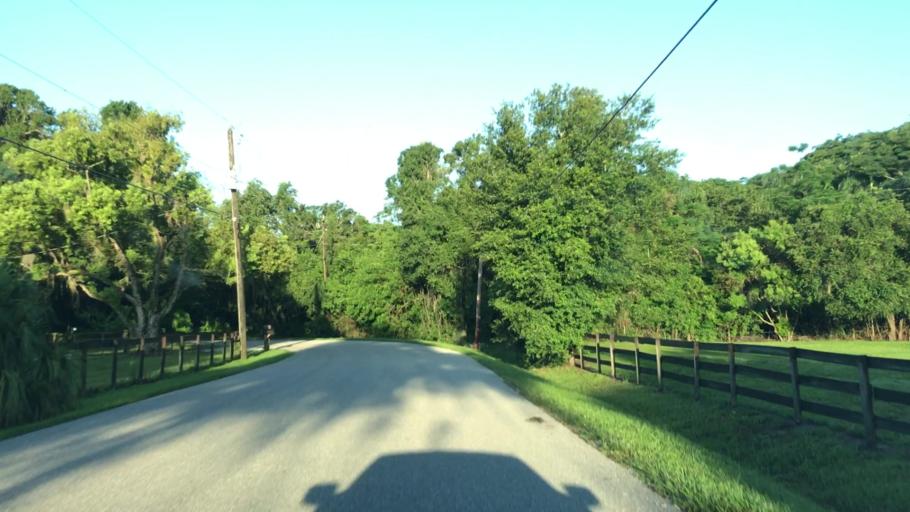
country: US
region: Florida
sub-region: Sarasota County
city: Fruitville
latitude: 27.3333
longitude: -82.4077
